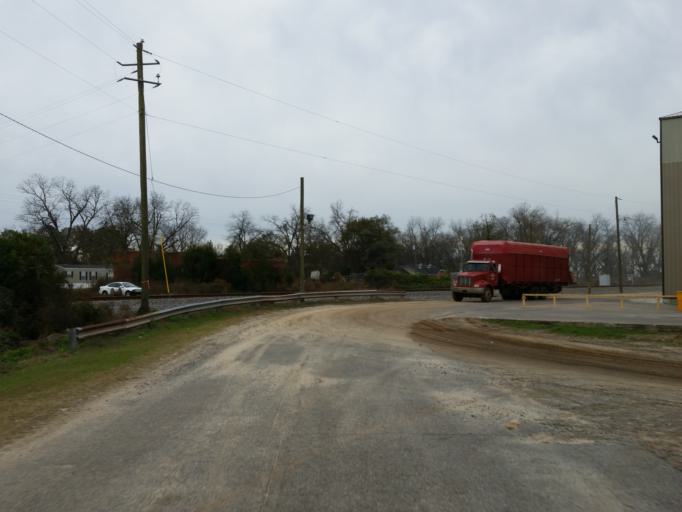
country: US
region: Georgia
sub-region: Dooly County
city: Vienna
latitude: 32.1549
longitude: -83.7718
